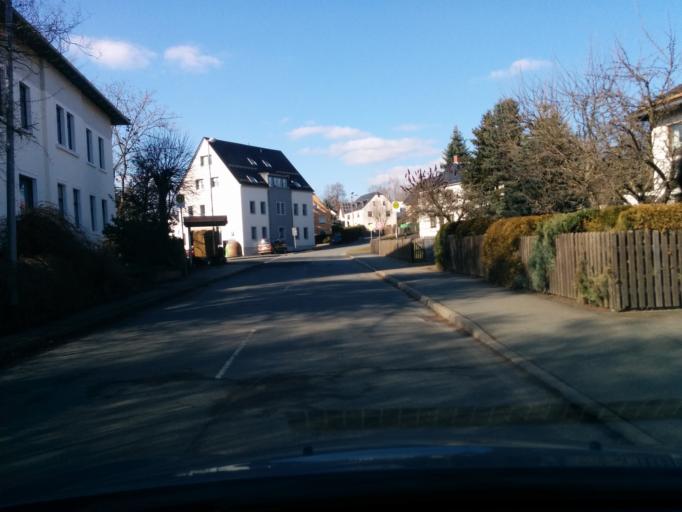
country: DE
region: Saxony
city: Neukirchen
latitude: 50.7863
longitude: 12.8488
